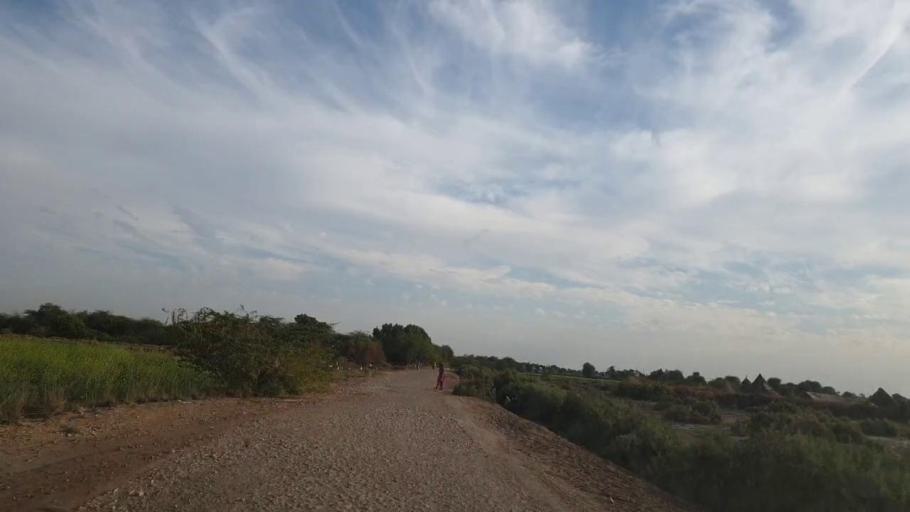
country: PK
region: Sindh
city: Pithoro
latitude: 25.6484
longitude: 69.2909
